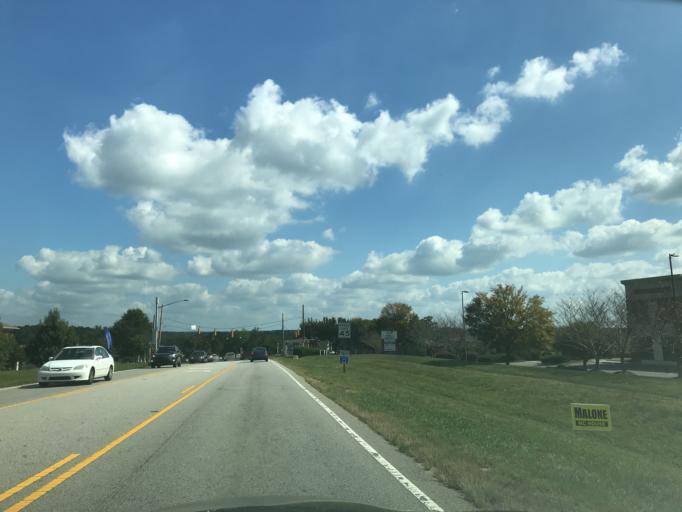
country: US
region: North Carolina
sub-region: Wake County
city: Wake Forest
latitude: 35.9506
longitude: -78.5201
